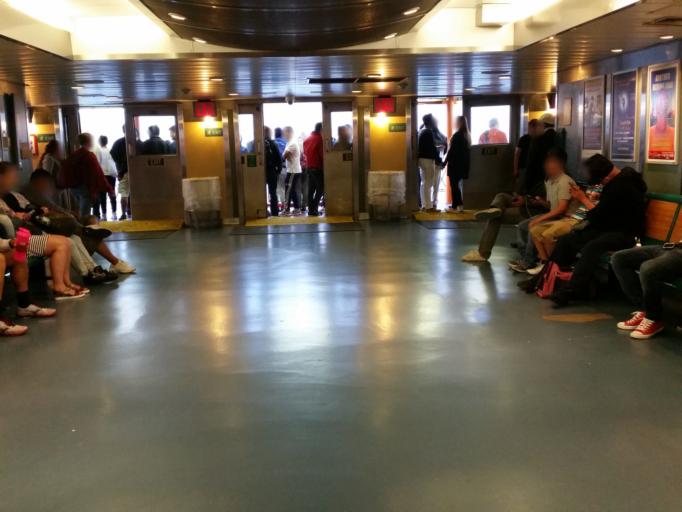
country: US
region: New Jersey
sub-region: Hudson County
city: Bayonne
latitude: 40.6453
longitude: -74.0692
